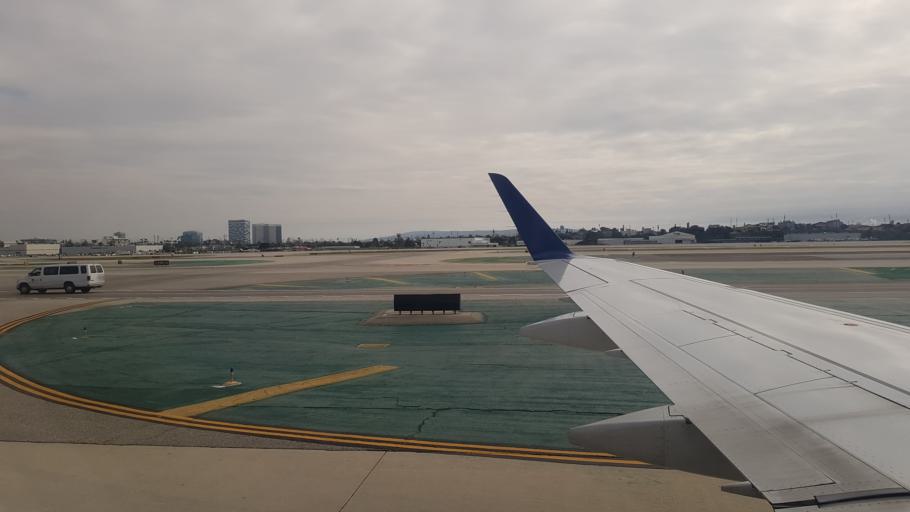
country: US
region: California
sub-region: Los Angeles County
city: El Segundo
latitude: 33.9387
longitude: -118.4093
